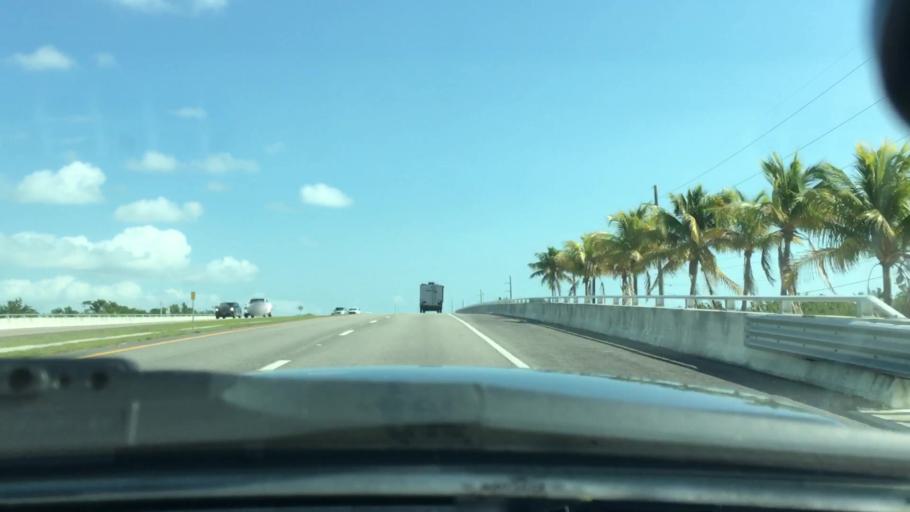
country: US
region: Florida
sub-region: Monroe County
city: Big Coppitt Key
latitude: 24.5879
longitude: -81.6926
